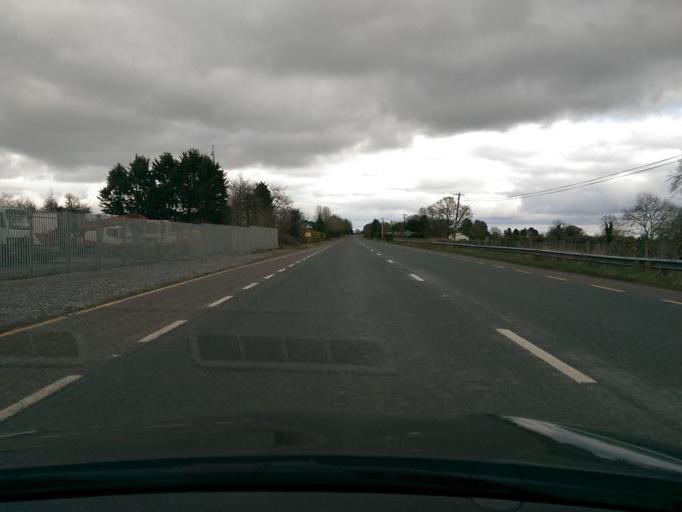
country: IE
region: Leinster
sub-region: An Iarmhi
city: Moate
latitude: 53.3966
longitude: -7.6664
